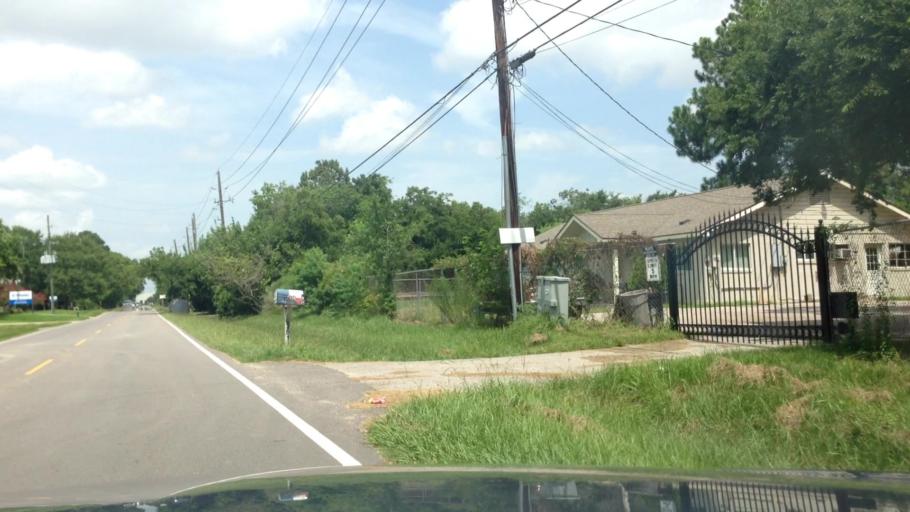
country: US
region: Texas
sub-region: Harris County
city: Jersey Village
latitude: 29.9104
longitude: -95.5443
